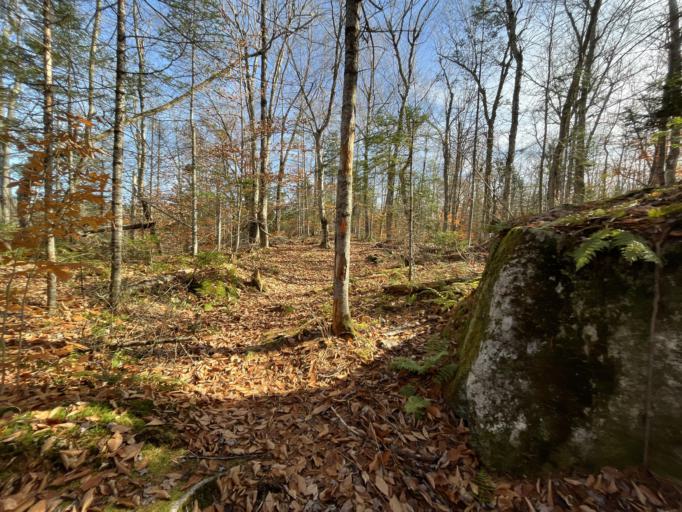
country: US
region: New Hampshire
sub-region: Merrimack County
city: New London
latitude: 43.3970
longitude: -71.9923
